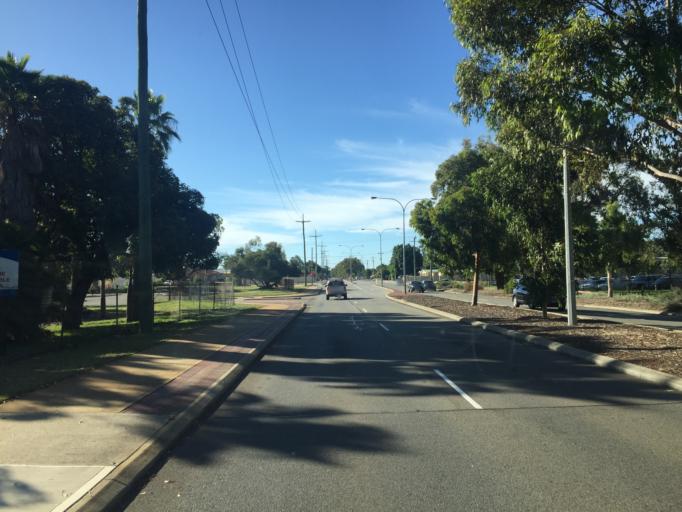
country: AU
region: Western Australia
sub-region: Belmont
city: Kewdale
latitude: -31.9692
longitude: 115.9442
